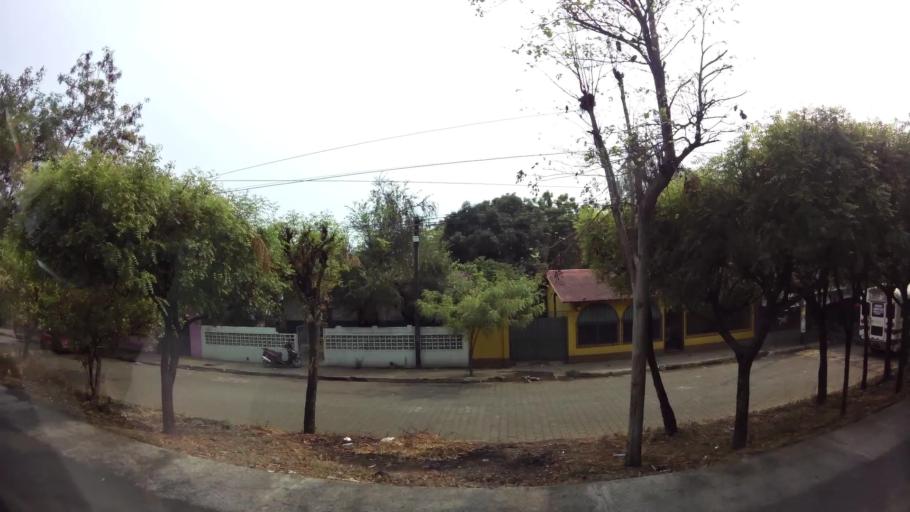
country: NI
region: Chinandega
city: Chinandega
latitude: 12.6372
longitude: -87.1386
